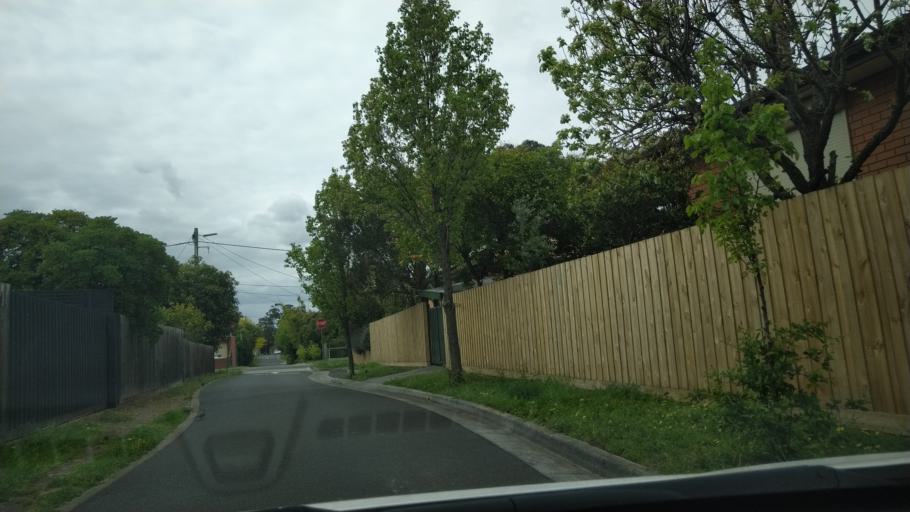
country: AU
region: Victoria
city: Hughesdale
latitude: -37.9073
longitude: 145.0800
